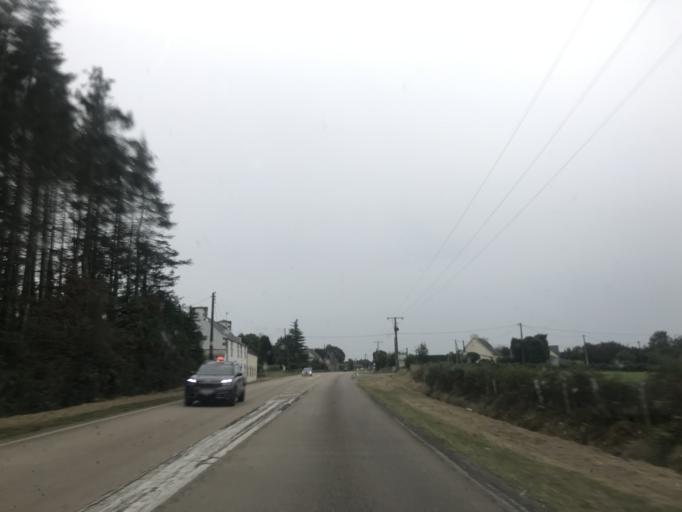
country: FR
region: Brittany
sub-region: Departement du Finistere
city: Plouneour-Menez
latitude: 48.4500
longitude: -3.8797
